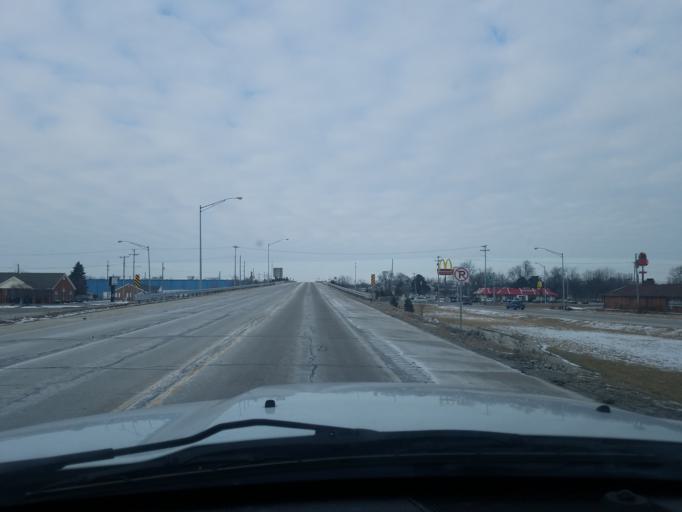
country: US
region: Indiana
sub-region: Randolph County
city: Winchester
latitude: 40.1706
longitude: -84.9669
